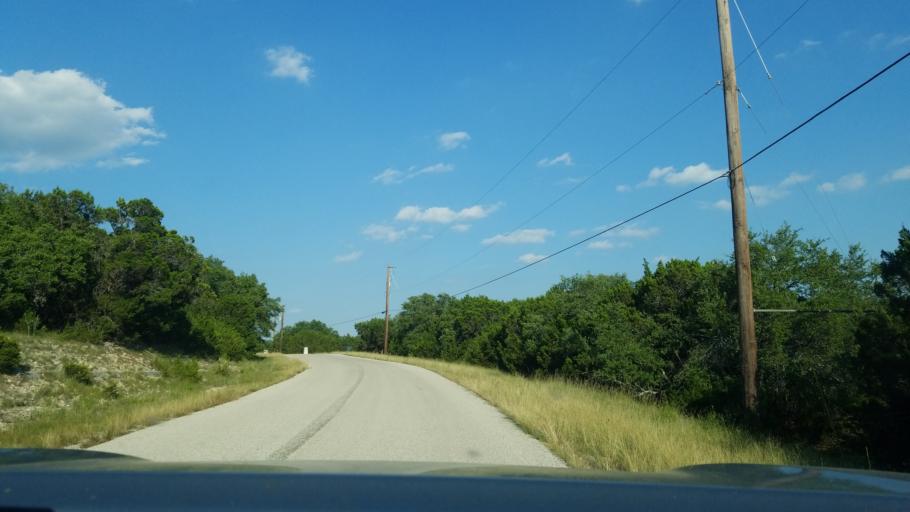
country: US
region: Texas
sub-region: Comal County
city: Bulverde
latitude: 29.7782
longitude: -98.4357
